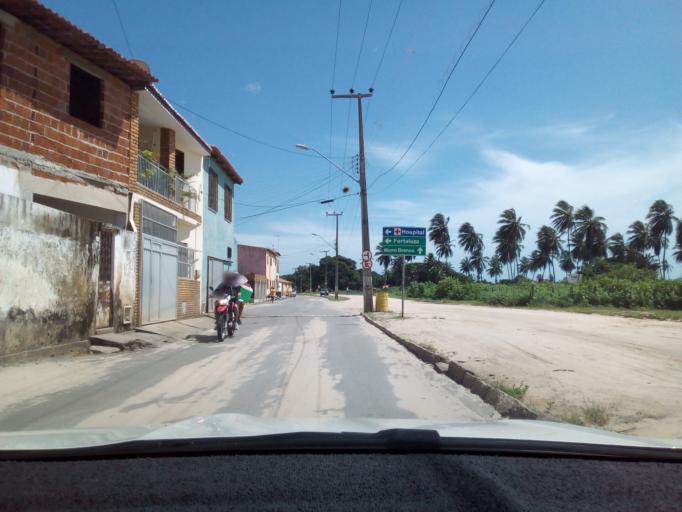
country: BR
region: Ceara
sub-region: Beberibe
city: Beberibe
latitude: -4.1830
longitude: -38.1256
